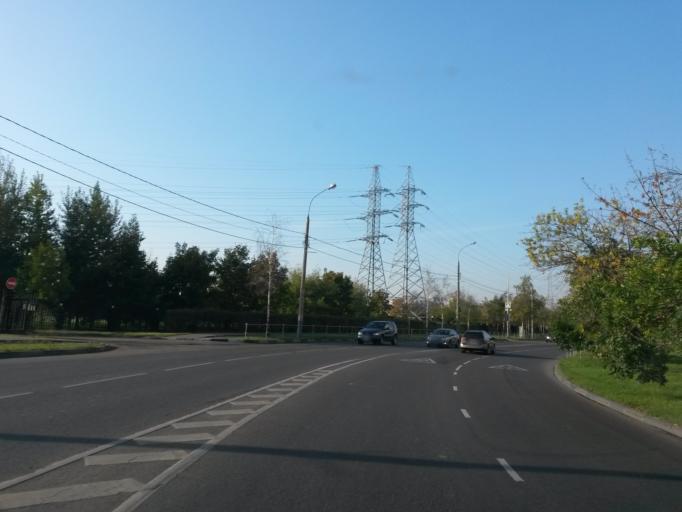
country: RU
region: Moscow
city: Brateyevo
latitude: 55.6495
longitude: 37.7672
